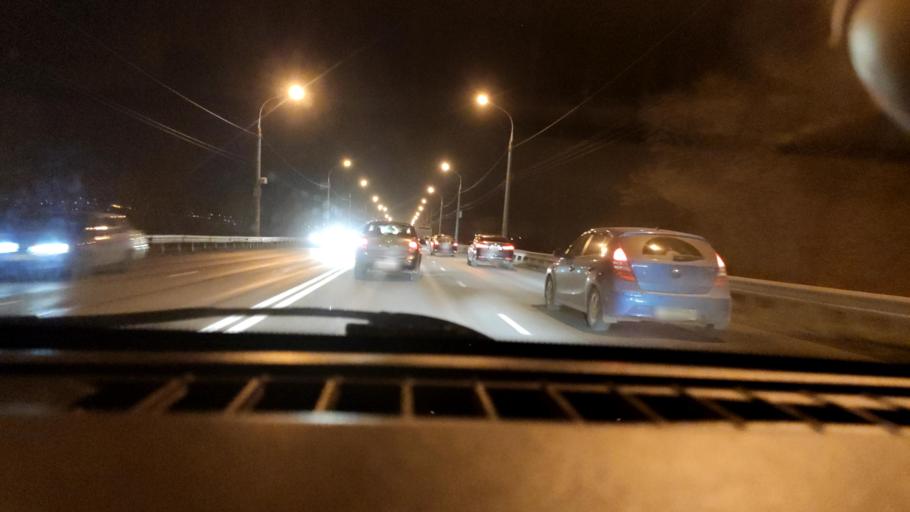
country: RU
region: Samara
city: Samara
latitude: 53.1542
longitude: 50.1892
